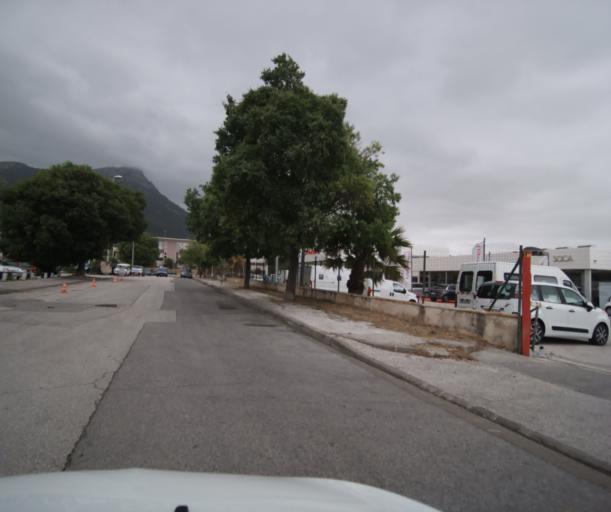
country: FR
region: Provence-Alpes-Cote d'Azur
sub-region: Departement du Var
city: La Garde
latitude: 43.1381
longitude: 6.0111
